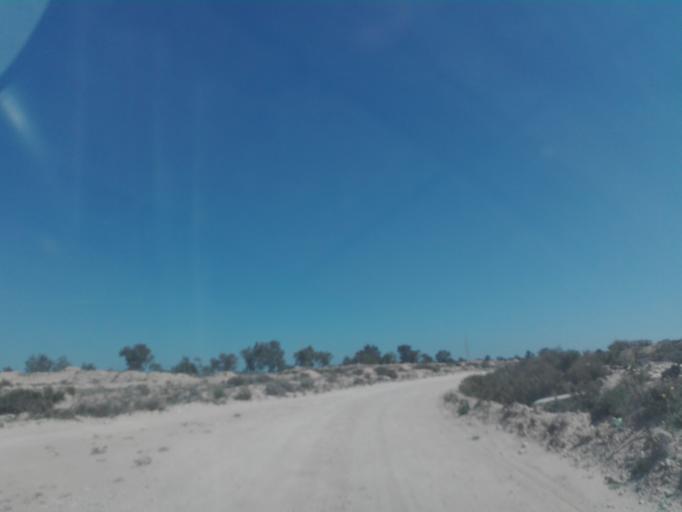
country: TN
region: Qabis
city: Gabes
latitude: 33.8752
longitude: 10.0251
